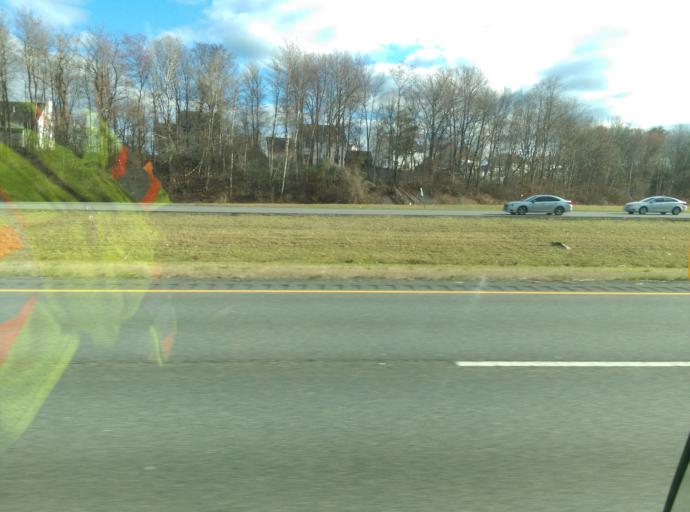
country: US
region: Massachusetts
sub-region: Essex County
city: Haverhill
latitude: 42.8026
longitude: -71.0489
